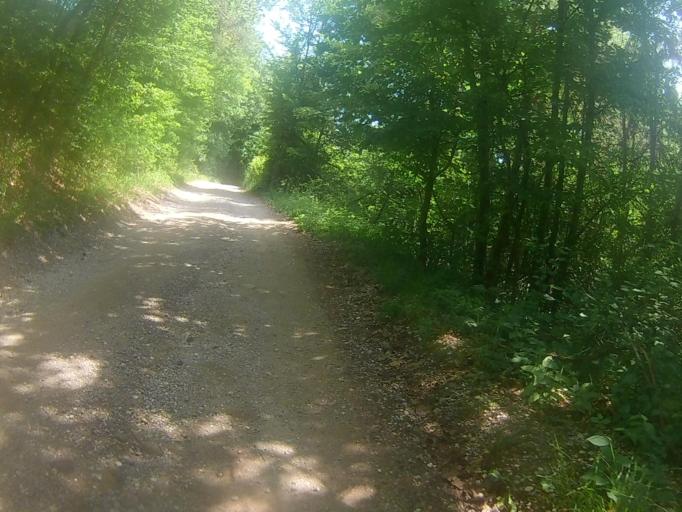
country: SI
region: Maribor
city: Bresternica
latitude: 46.5961
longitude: 15.5906
